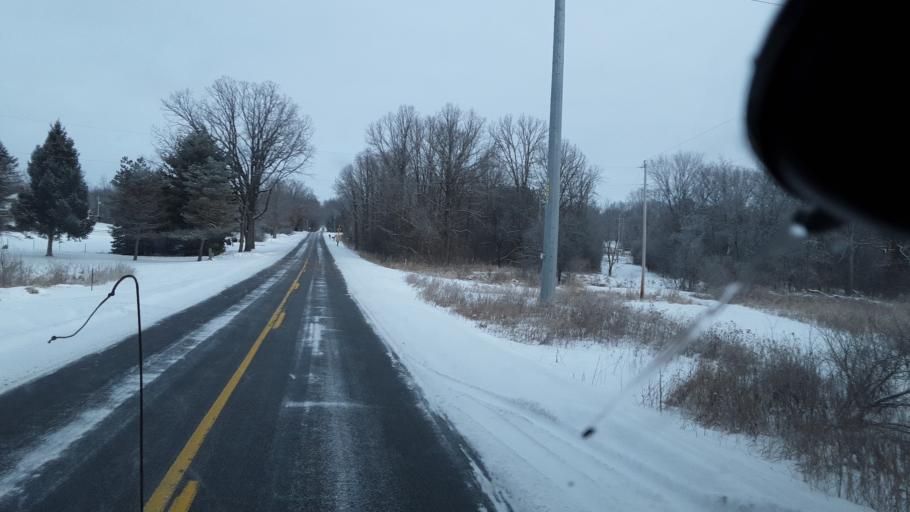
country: US
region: Michigan
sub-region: Jackson County
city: Jackson
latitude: 42.3271
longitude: -84.4828
